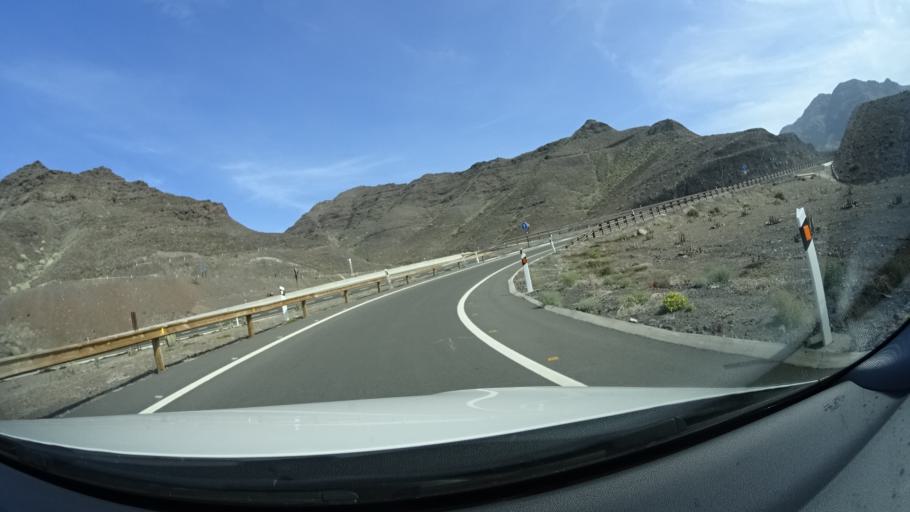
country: ES
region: Canary Islands
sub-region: Provincia de Las Palmas
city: San Nicolas
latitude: 28.0089
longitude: -15.7884
